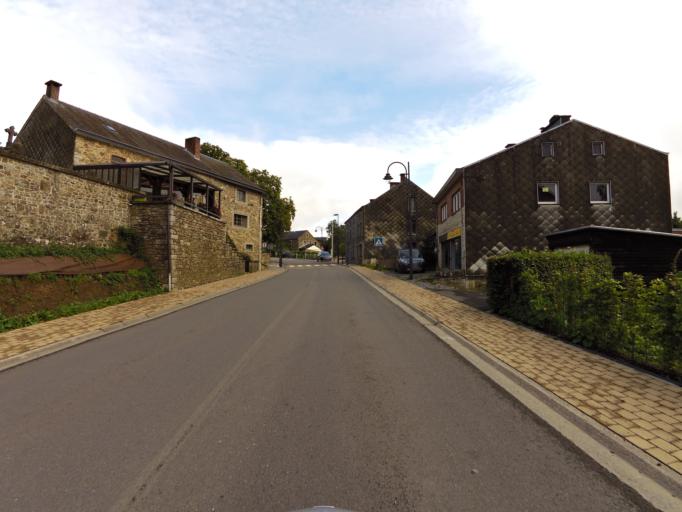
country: BE
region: Wallonia
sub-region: Province du Luxembourg
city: Erezee
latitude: 50.2915
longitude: 5.5588
